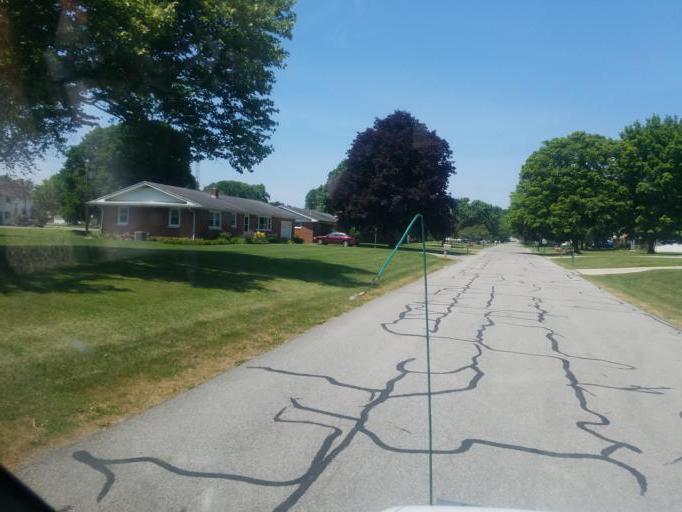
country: US
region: Ohio
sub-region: Logan County
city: West Liberty
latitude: 40.2570
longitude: -83.7494
